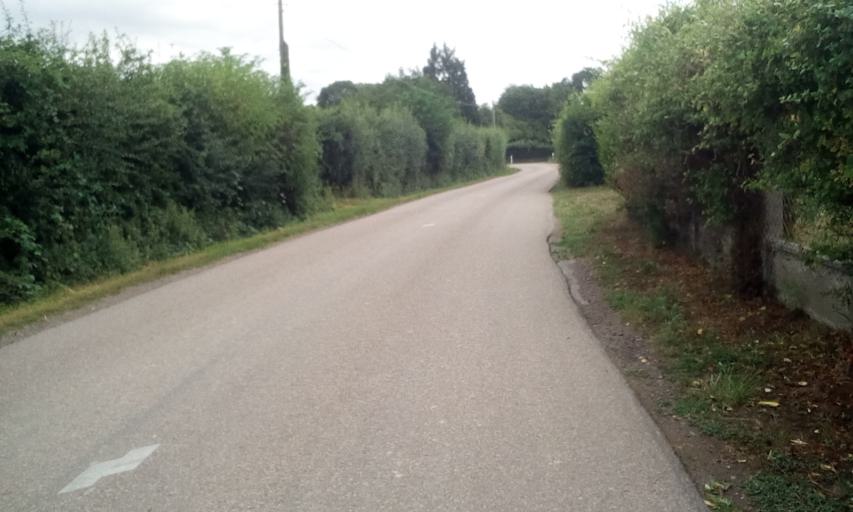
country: FR
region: Lower Normandy
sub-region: Departement du Calvados
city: Bavent
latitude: 49.2140
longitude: -0.1795
